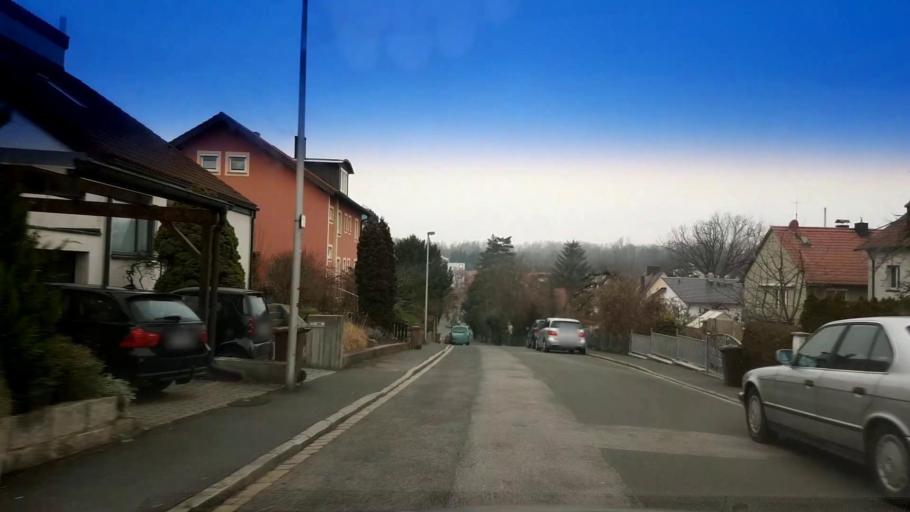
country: DE
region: Bavaria
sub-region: Upper Franconia
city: Bischberg
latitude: 49.9016
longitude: 10.8562
